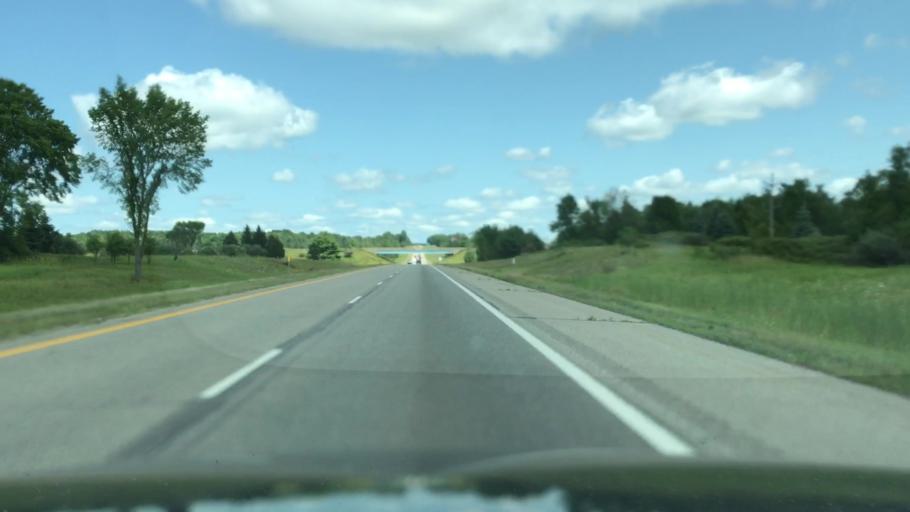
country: US
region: Michigan
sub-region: Mecosta County
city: Big Rapids
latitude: 43.7111
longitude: -85.5294
